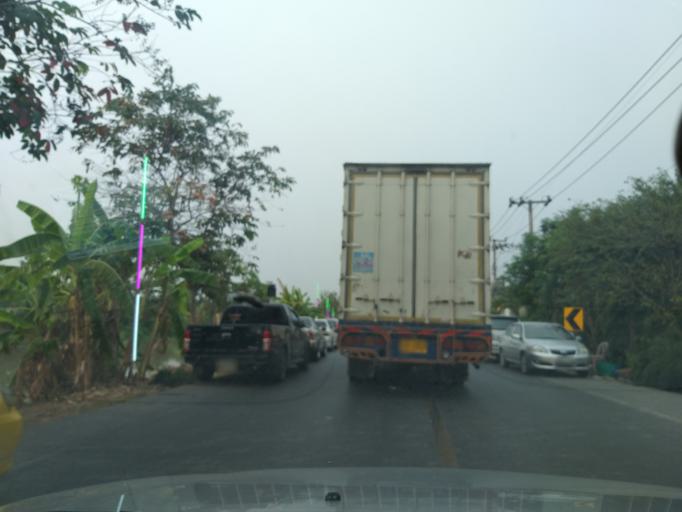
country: TH
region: Bangkok
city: Nong Chok
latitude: 13.8754
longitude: 100.8838
